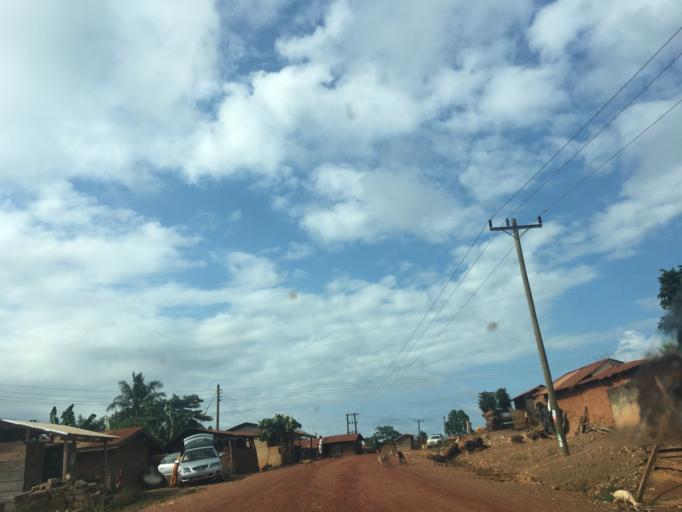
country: GH
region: Western
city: Wassa-Akropong
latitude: 5.9585
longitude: -2.4307
